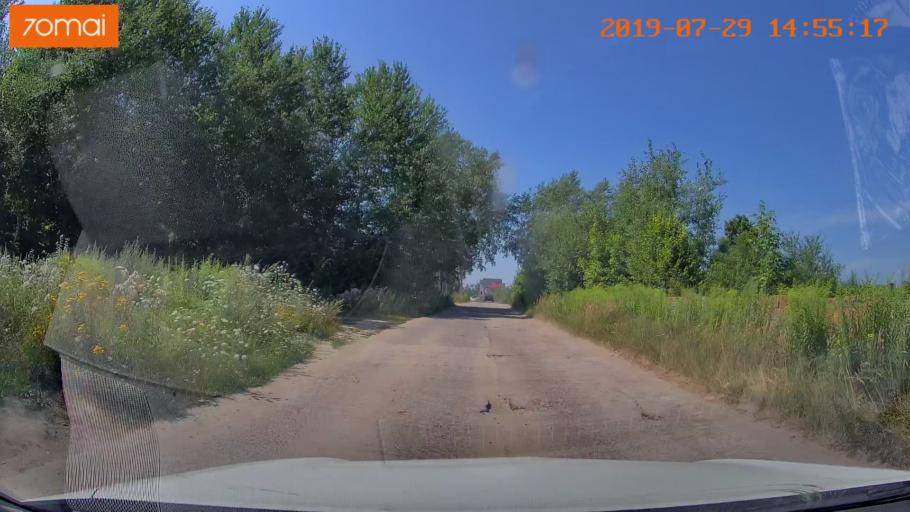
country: RU
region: Kaliningrad
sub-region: Gorod Kaliningrad
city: Baltiysk
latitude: 54.6788
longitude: 19.9268
